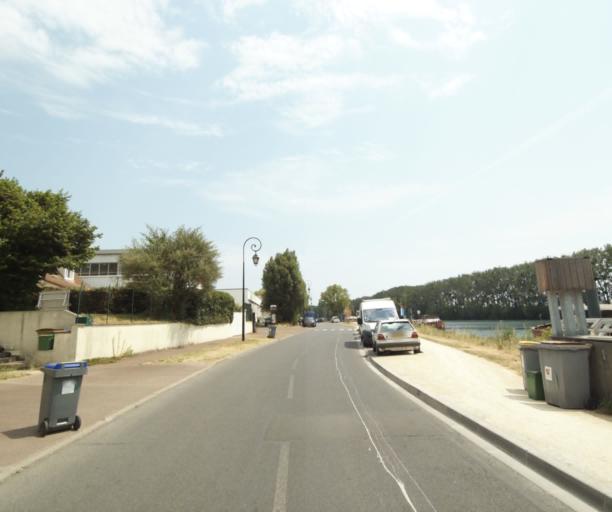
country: FR
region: Ile-de-France
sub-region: Departement des Yvelines
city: Conflans-Sainte-Honorine
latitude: 48.9916
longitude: 2.1100
